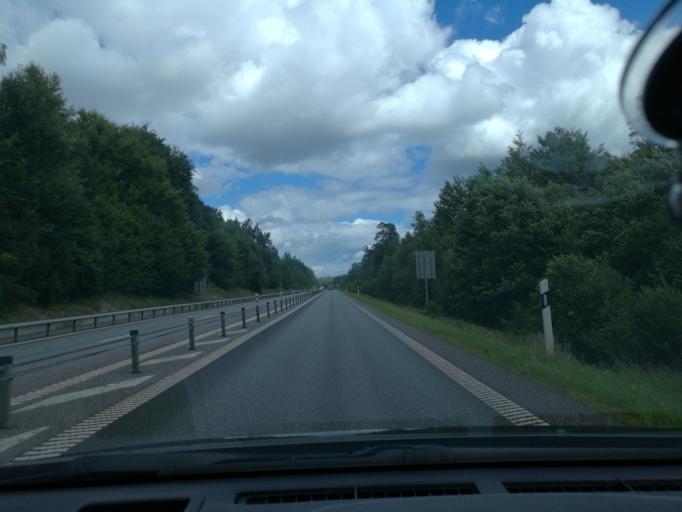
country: SE
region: Skane
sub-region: Hassleholms Kommun
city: Hastveda
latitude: 56.2303
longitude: 13.8909
